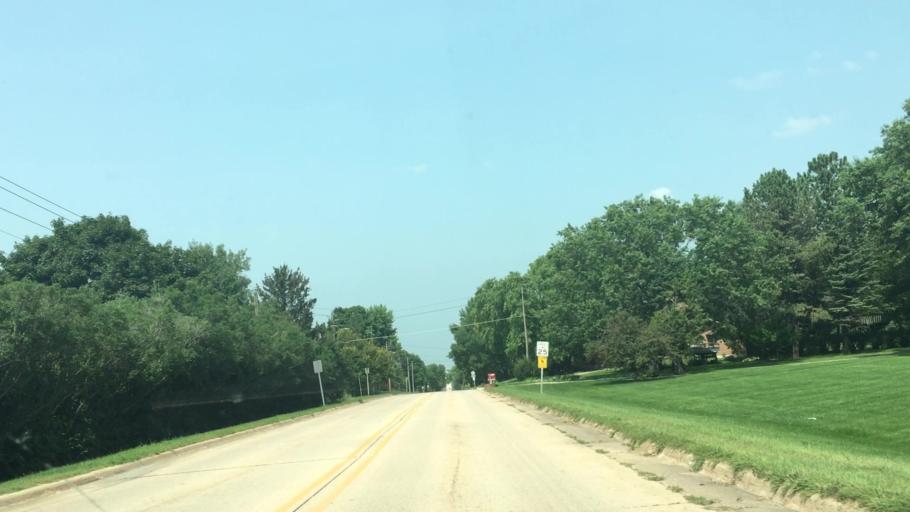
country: US
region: Iowa
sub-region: Fayette County
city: Oelwein
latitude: 42.6765
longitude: -91.8936
